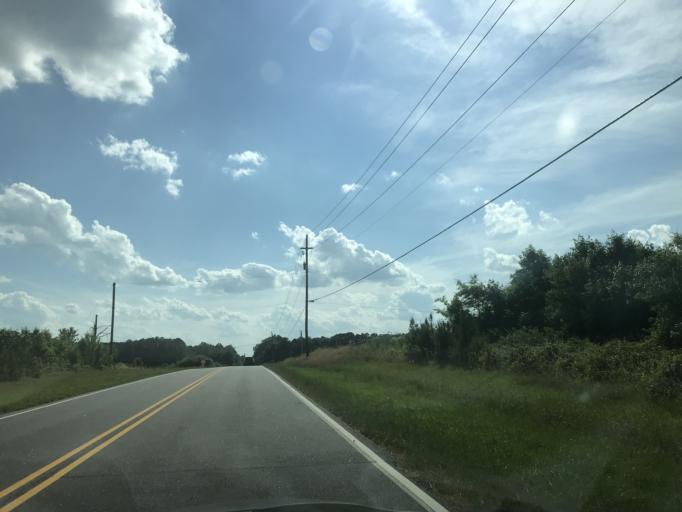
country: US
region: North Carolina
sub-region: Nash County
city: Spring Hope
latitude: 35.9552
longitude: -78.0831
